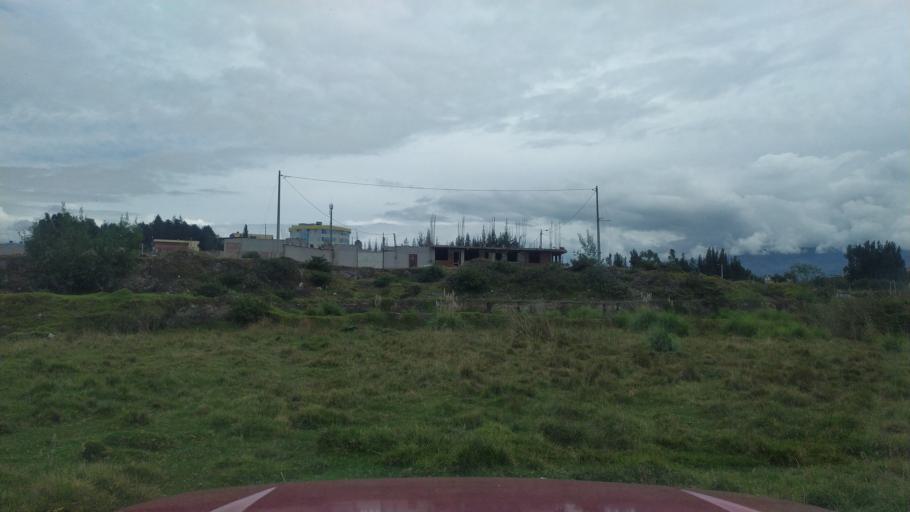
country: EC
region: Chimborazo
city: Riobamba
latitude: -1.6534
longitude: -78.6391
